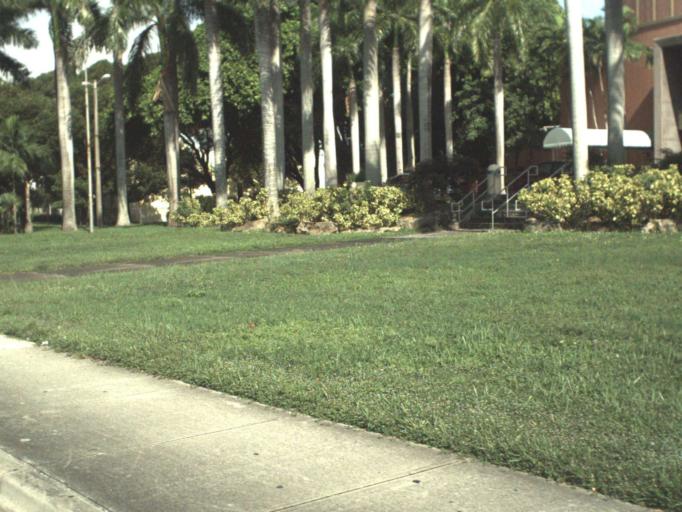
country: US
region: Florida
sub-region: Miami-Dade County
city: Allapattah
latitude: 25.7723
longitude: -80.2409
